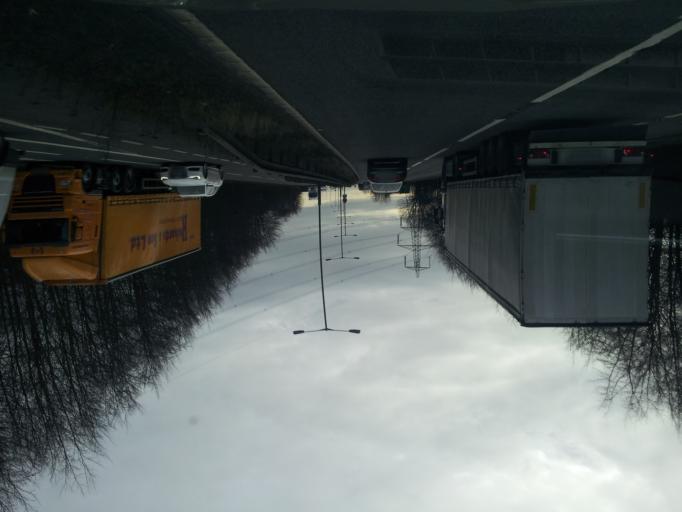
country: GB
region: England
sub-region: Lincolnshire
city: Grantham
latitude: 52.8736
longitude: -0.6312
